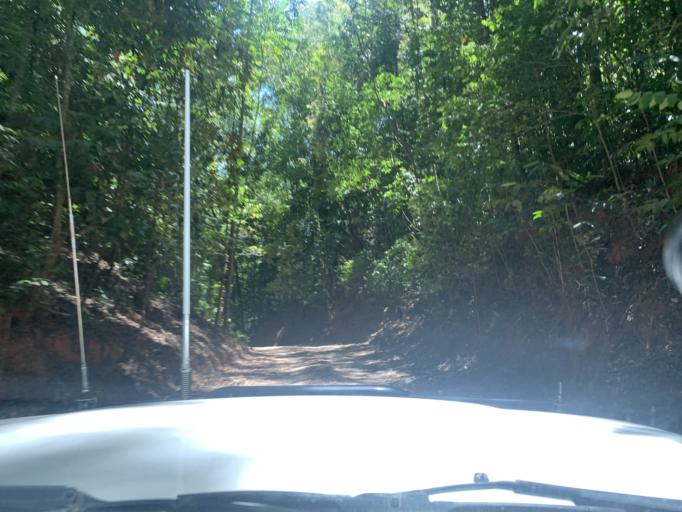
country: AU
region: Queensland
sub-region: Cairns
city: Redlynch
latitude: -16.9590
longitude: 145.6451
